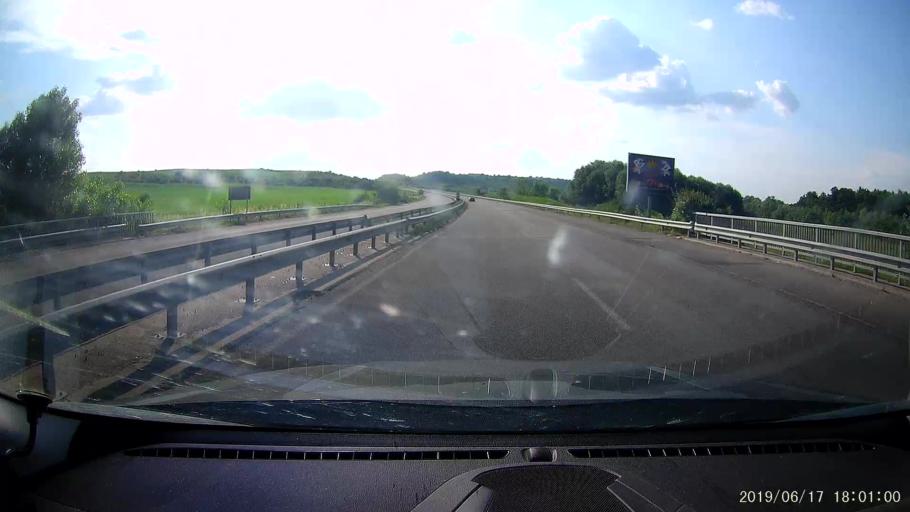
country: BG
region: Khaskovo
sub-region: Obshtina Svilengrad
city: Svilengrad
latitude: 41.7428
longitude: 26.2672
